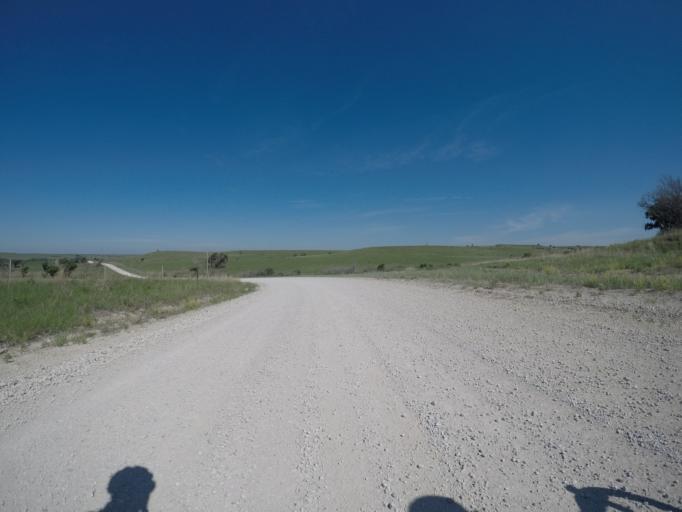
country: US
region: Kansas
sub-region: Wabaunsee County
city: Alma
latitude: 39.0150
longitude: -96.1142
